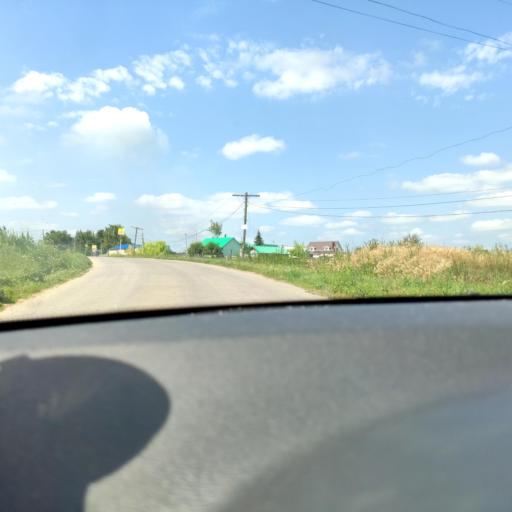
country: RU
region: Samara
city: Kinel'
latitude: 53.3403
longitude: 50.5253
